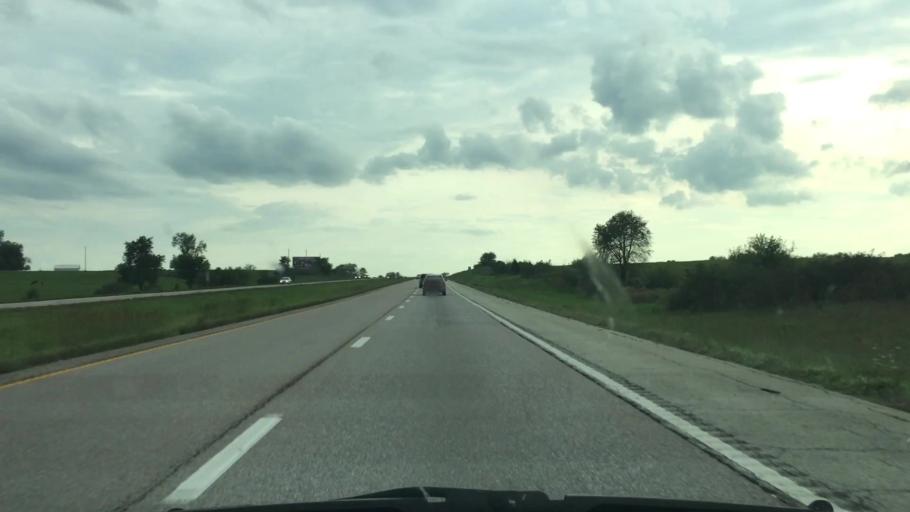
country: US
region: Missouri
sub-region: Clinton County
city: Lathrop
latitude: 39.5280
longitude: -94.2796
